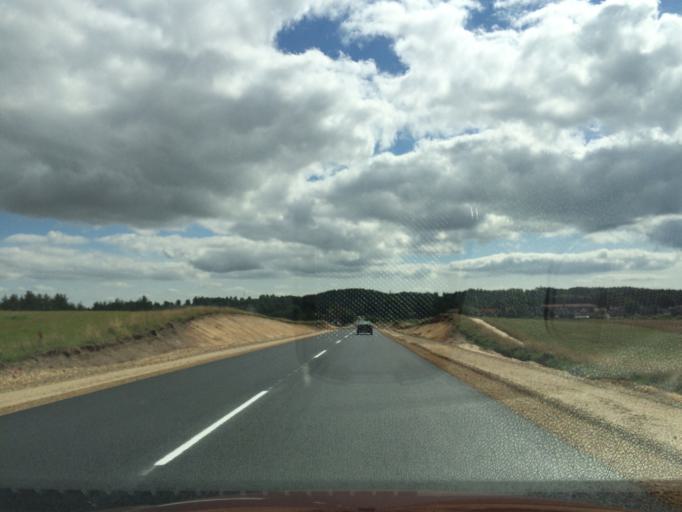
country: DK
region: Central Jutland
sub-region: Silkeborg Kommune
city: Svejbaek
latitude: 56.1852
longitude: 9.6355
